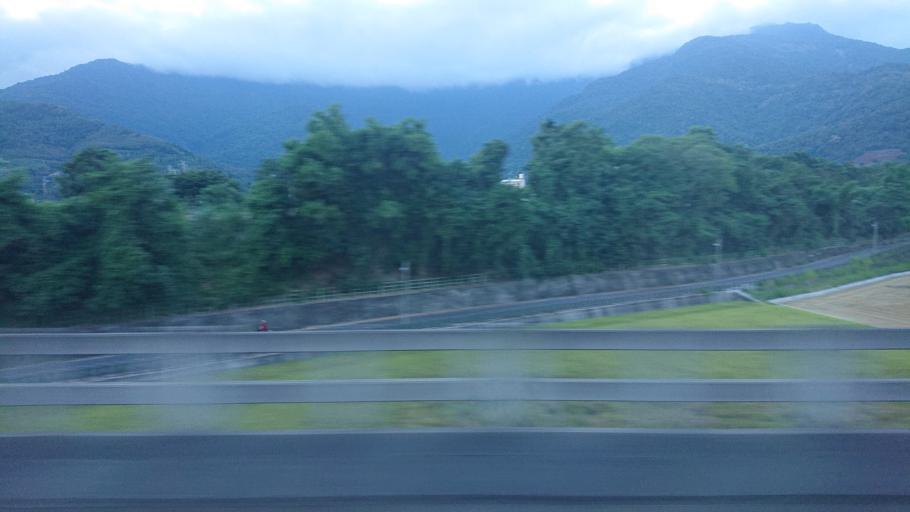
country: TW
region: Taiwan
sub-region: Taitung
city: Taitung
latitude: 23.0390
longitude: 121.1623
